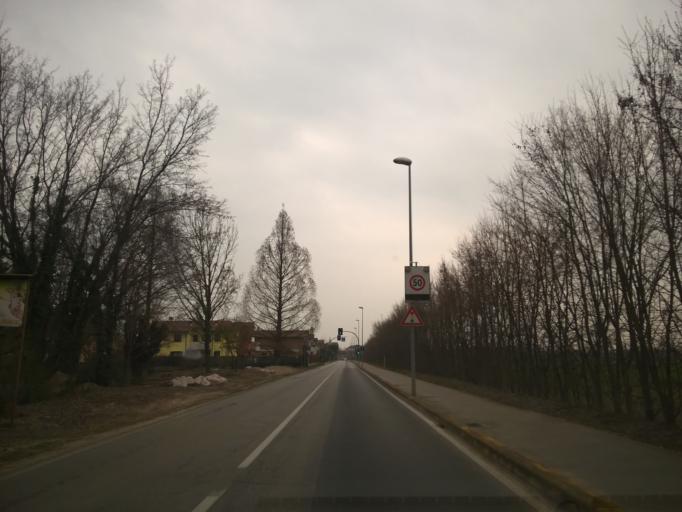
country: IT
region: Veneto
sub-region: Provincia di Vicenza
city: Sandrigo
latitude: 45.6445
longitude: 11.6071
